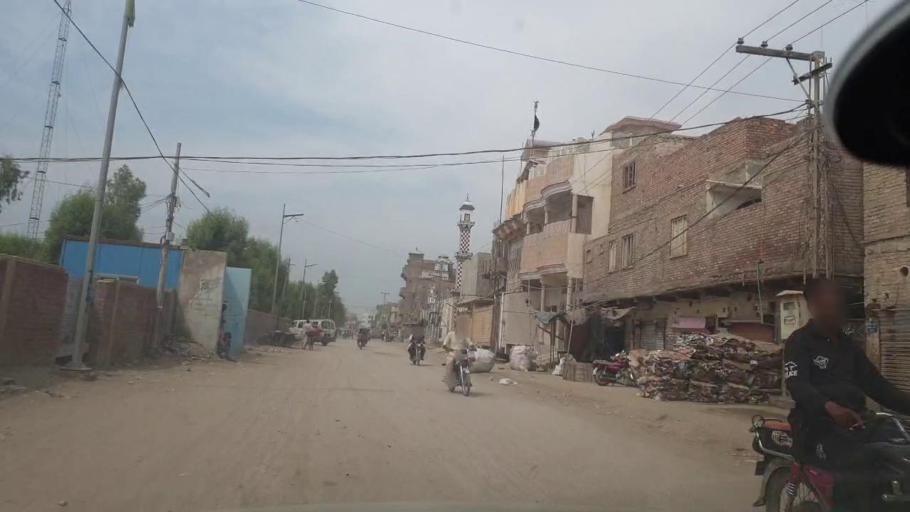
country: PK
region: Sindh
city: Jacobabad
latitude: 28.2745
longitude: 68.4380
